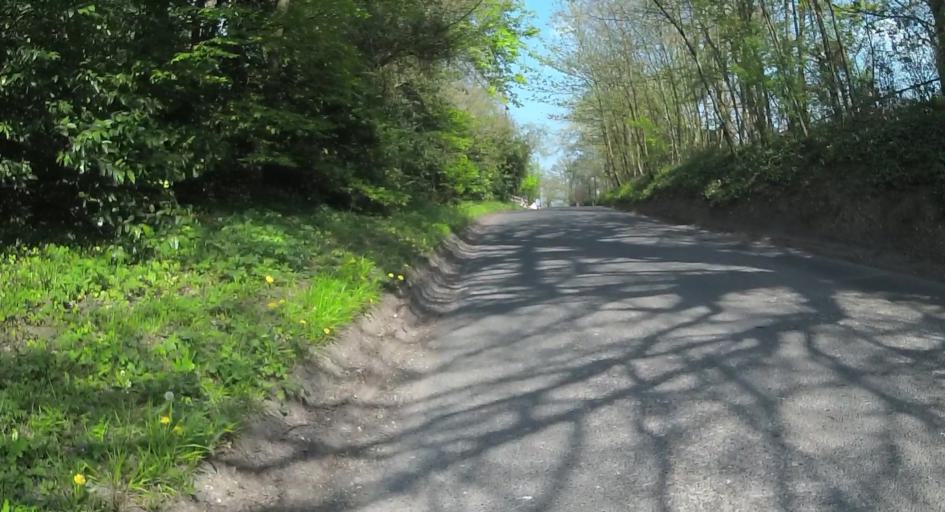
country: GB
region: England
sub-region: Hampshire
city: Basingstoke
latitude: 51.2964
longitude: -1.1025
